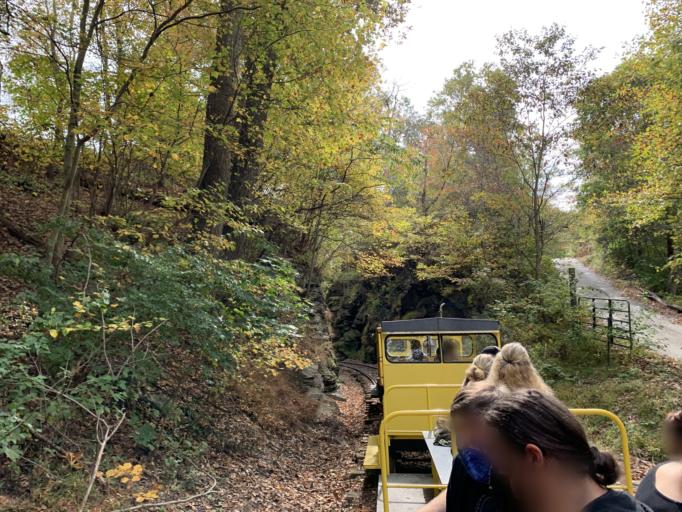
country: US
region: Pennsylvania
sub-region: York County
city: Susquehanna Trails
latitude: 39.8142
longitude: -76.4791
